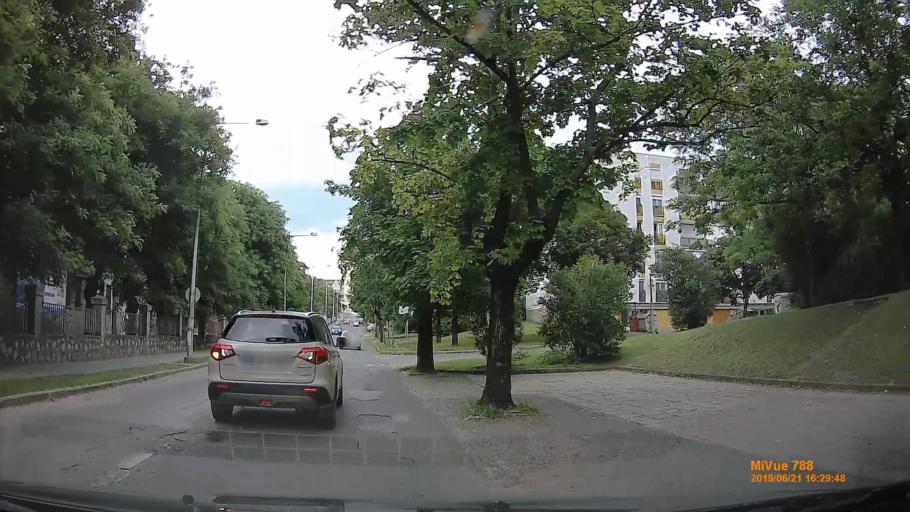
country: HU
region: Baranya
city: Pecs
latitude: 46.0732
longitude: 18.2083
